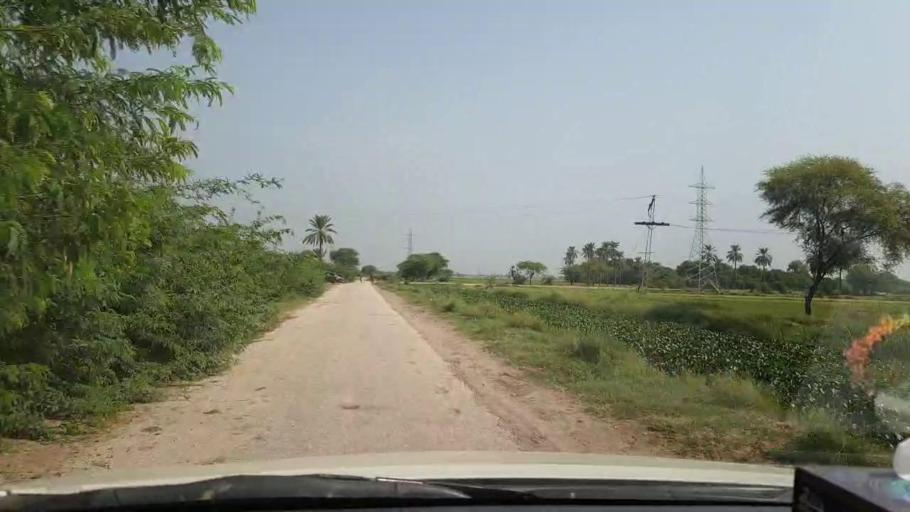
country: PK
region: Sindh
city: Shikarpur
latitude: 27.9791
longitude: 68.6641
